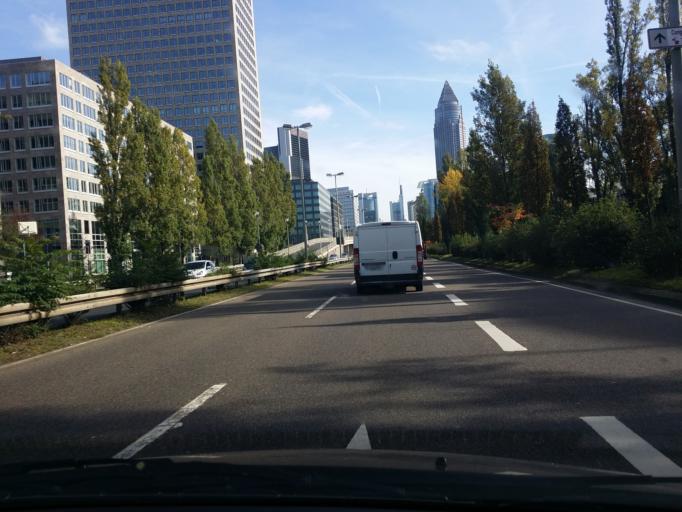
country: DE
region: Hesse
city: Niederrad
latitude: 50.1144
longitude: 8.6396
